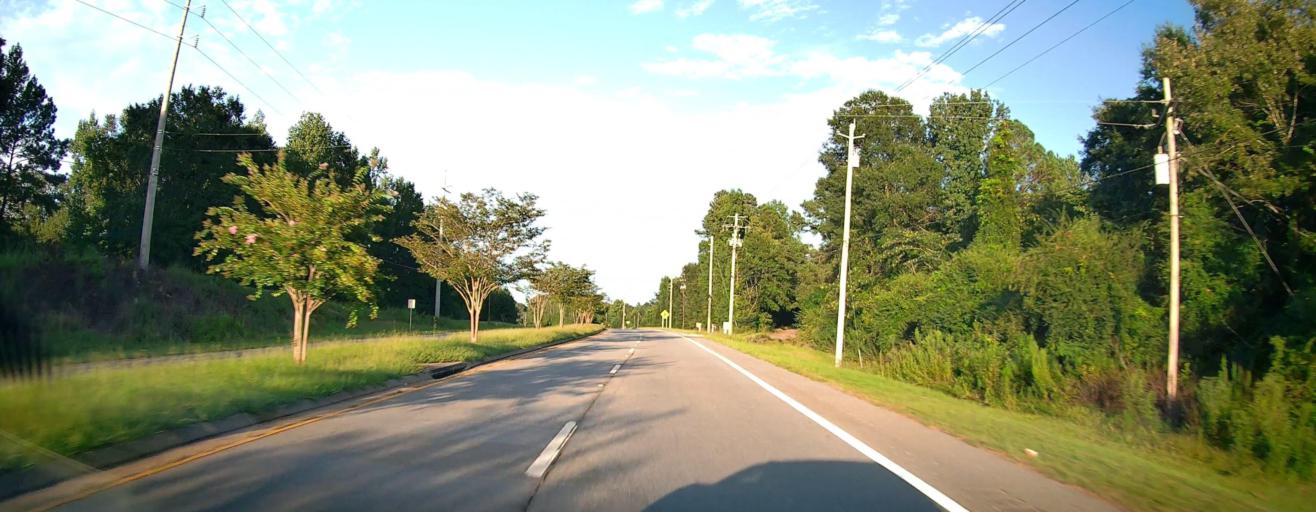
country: US
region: Georgia
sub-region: Muscogee County
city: Columbus
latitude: 32.5253
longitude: -84.8630
